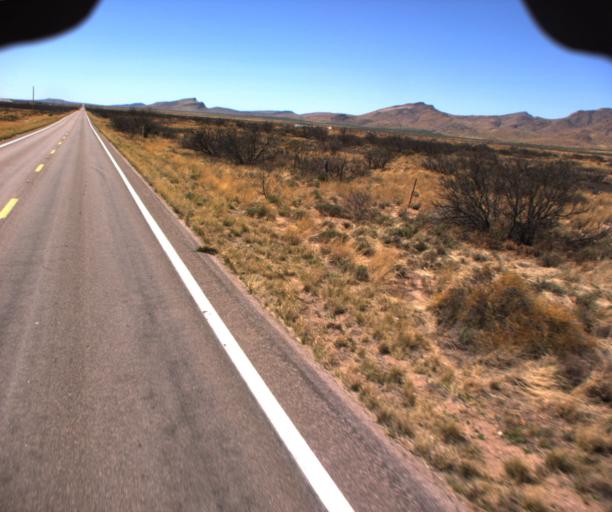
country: US
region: Arizona
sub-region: Cochise County
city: Douglas
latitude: 31.7457
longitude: -109.0945
